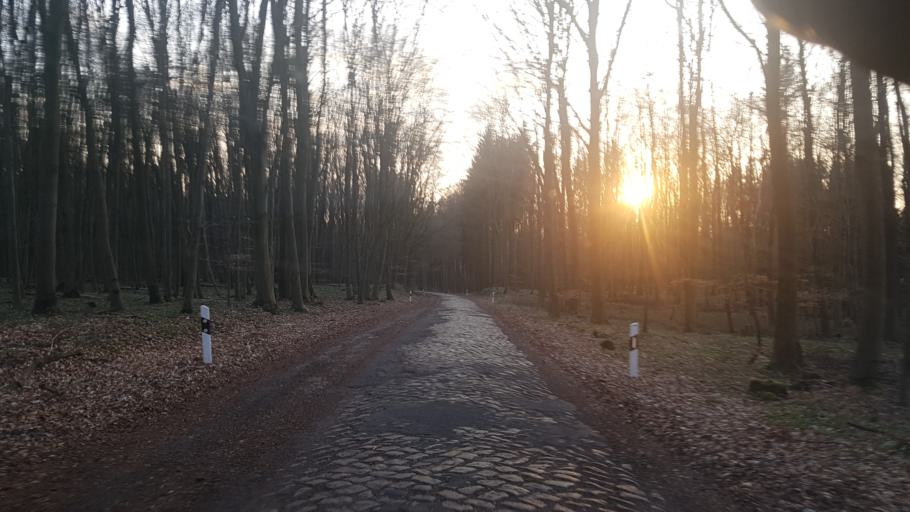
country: DE
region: Brandenburg
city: Gramzow
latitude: 53.1951
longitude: 13.9297
